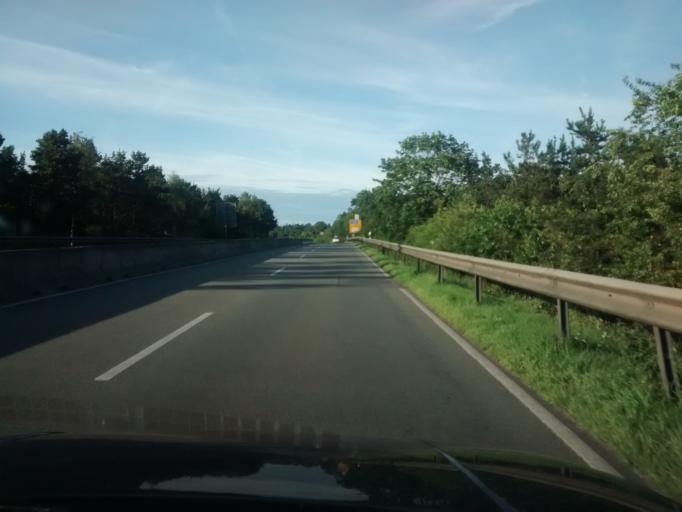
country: DE
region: Lower Saxony
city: Meppen
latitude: 52.7095
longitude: 7.2922
